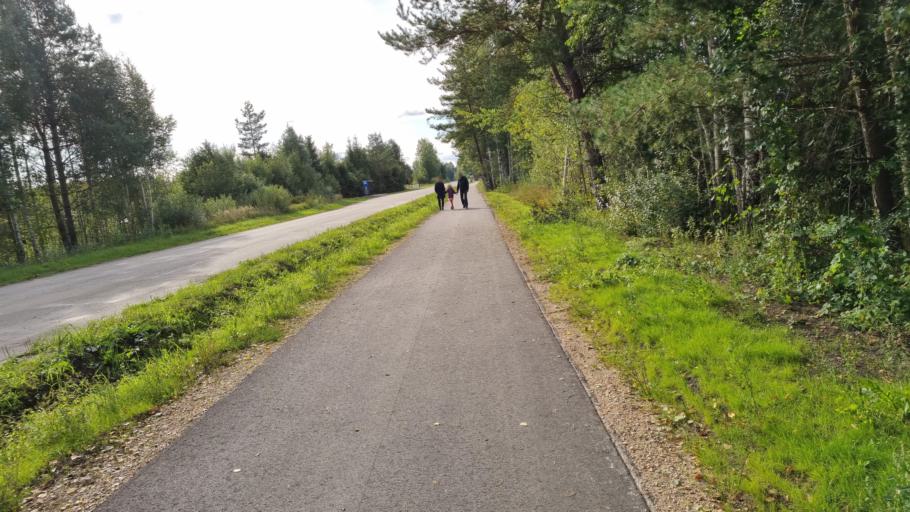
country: LV
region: Olaine
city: Olaine
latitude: 56.6994
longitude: 24.0712
